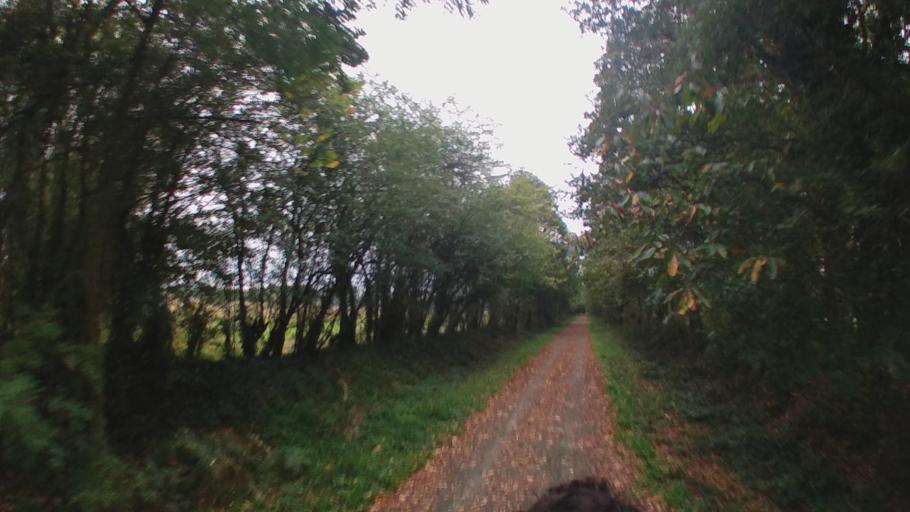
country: FR
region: Pays de la Loire
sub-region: Departement de la Mayenne
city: Aron
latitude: 48.3410
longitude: -0.5675
